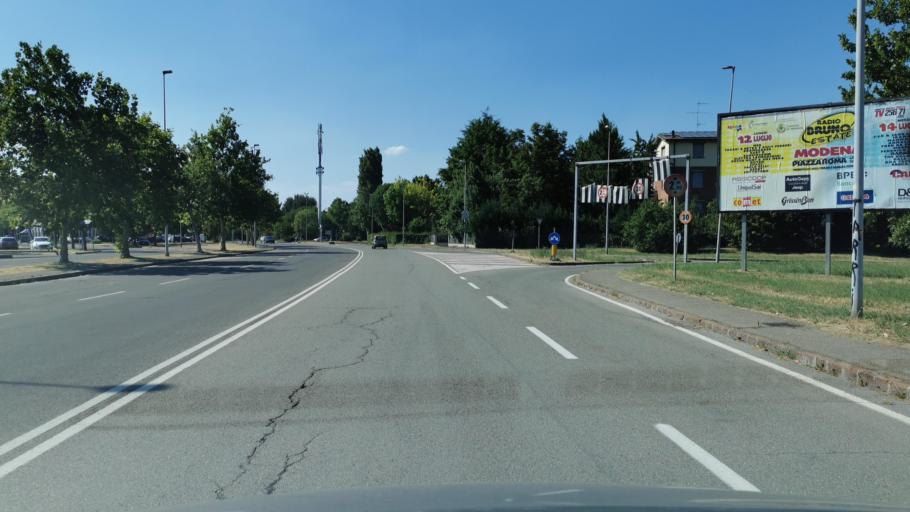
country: IT
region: Emilia-Romagna
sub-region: Provincia di Modena
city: Modena
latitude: 44.6210
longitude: 10.9292
